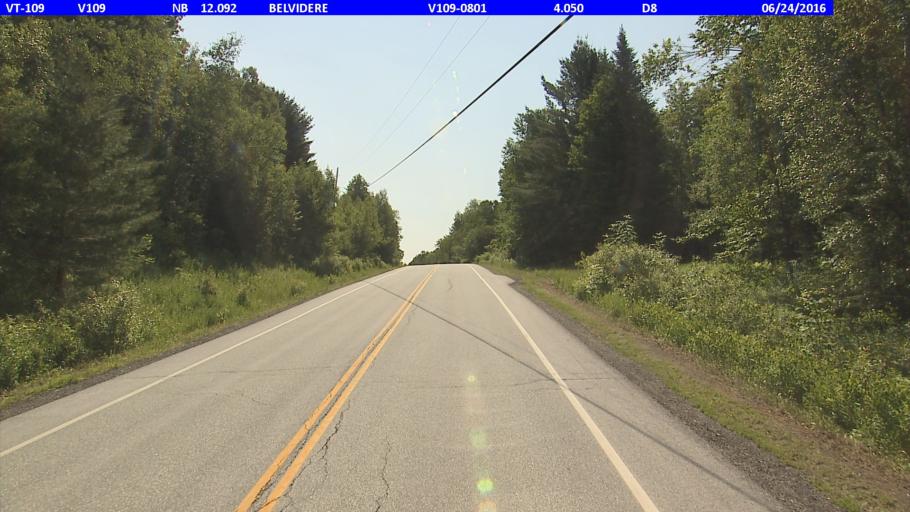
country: US
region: Vermont
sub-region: Lamoille County
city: Johnson
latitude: 44.7606
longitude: -72.6755
